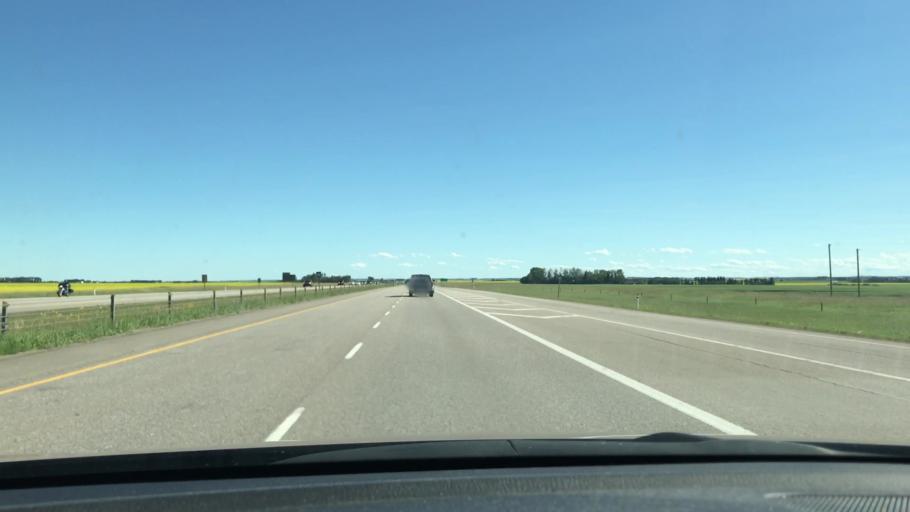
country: CA
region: Alberta
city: Didsbury
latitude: 51.6599
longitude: -114.0257
